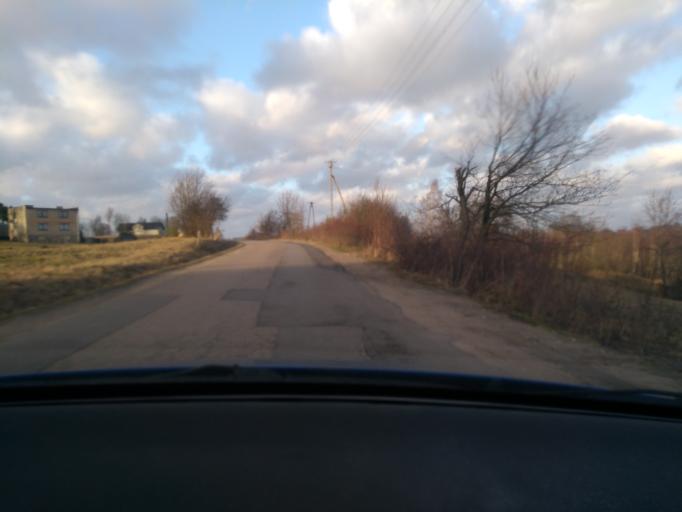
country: PL
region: Pomeranian Voivodeship
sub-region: Powiat kartuski
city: Kartuzy
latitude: 54.3830
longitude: 18.2203
